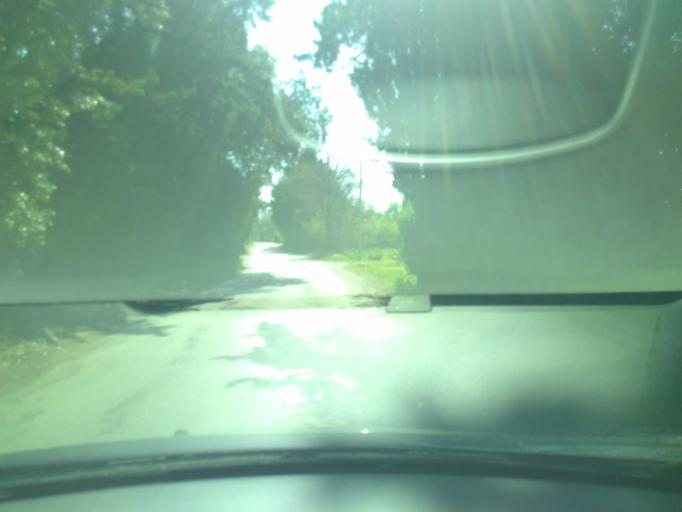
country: FR
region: Provence-Alpes-Cote d'Azur
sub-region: Departement du Vaucluse
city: Caromb
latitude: 44.0771
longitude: 5.0850
